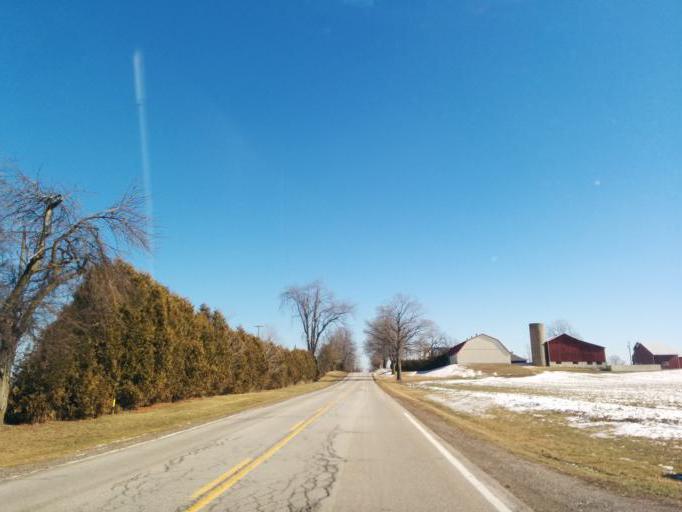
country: CA
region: Ontario
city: Brant
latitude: 43.0198
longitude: -80.3956
